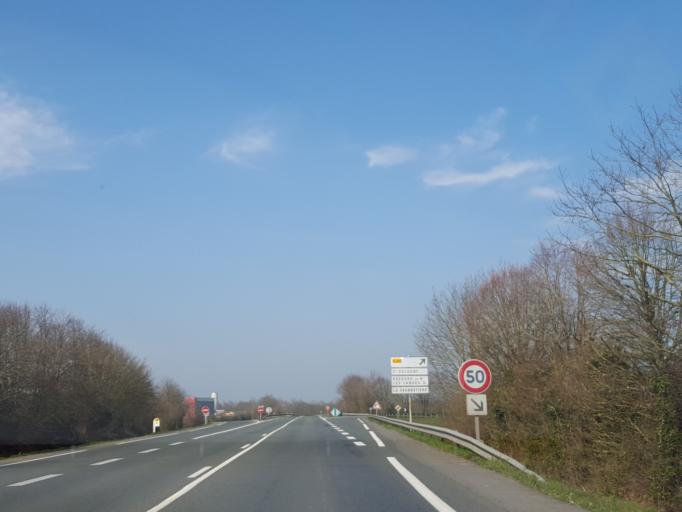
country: FR
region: Pays de la Loire
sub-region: Departement de la Vendee
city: Saint-Fulgent
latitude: 46.8574
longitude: -1.1697
